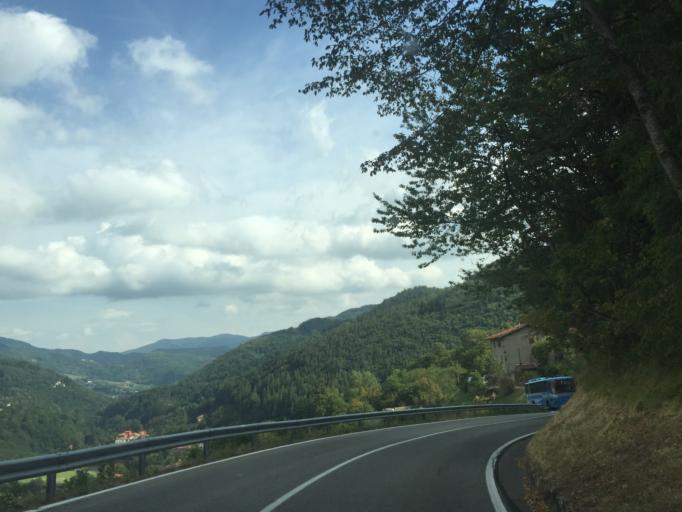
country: IT
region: Tuscany
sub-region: Provincia di Pistoia
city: Cutigliano
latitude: 44.1065
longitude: 10.7410
